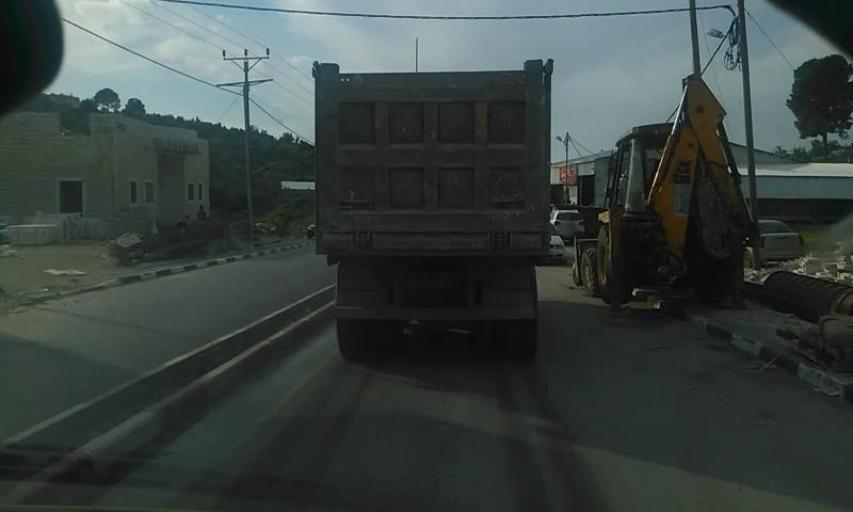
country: PS
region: West Bank
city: Bayt Ula
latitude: 31.5927
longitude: 35.0273
